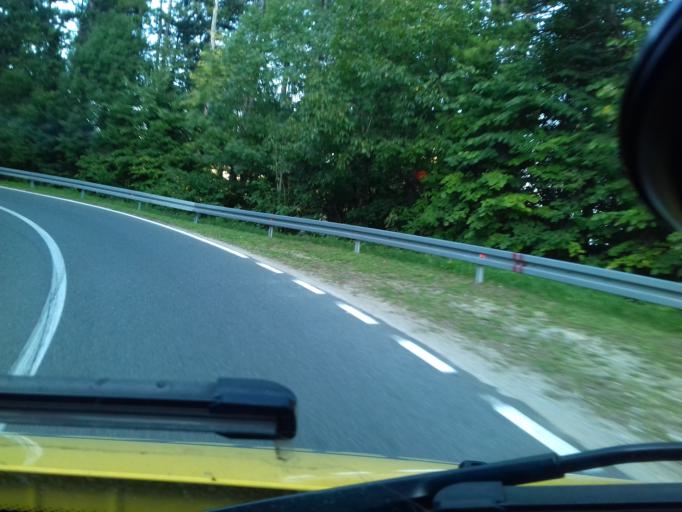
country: BA
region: Federation of Bosnia and Herzegovina
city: Ostrozac
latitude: 44.9031
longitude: 15.9336
